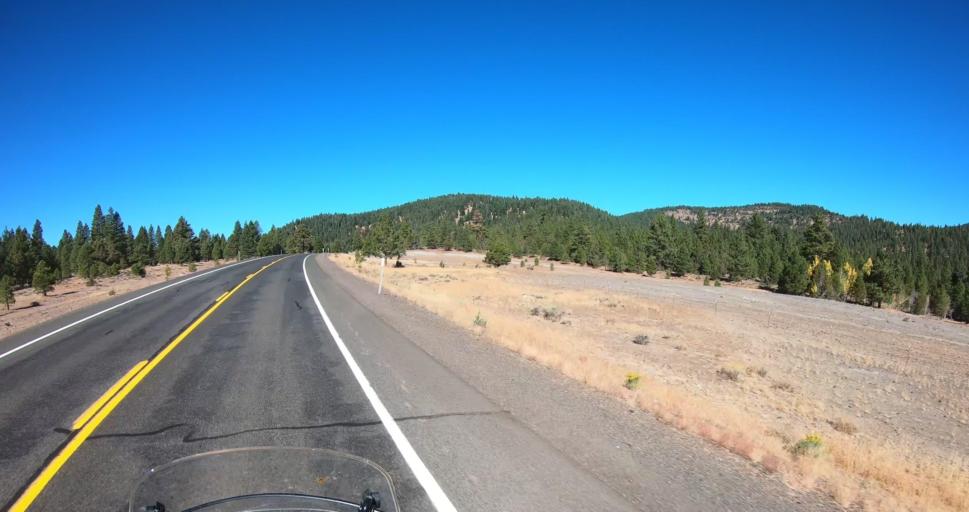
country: US
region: Oregon
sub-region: Lake County
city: Lakeview
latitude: 42.2274
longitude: -120.2551
